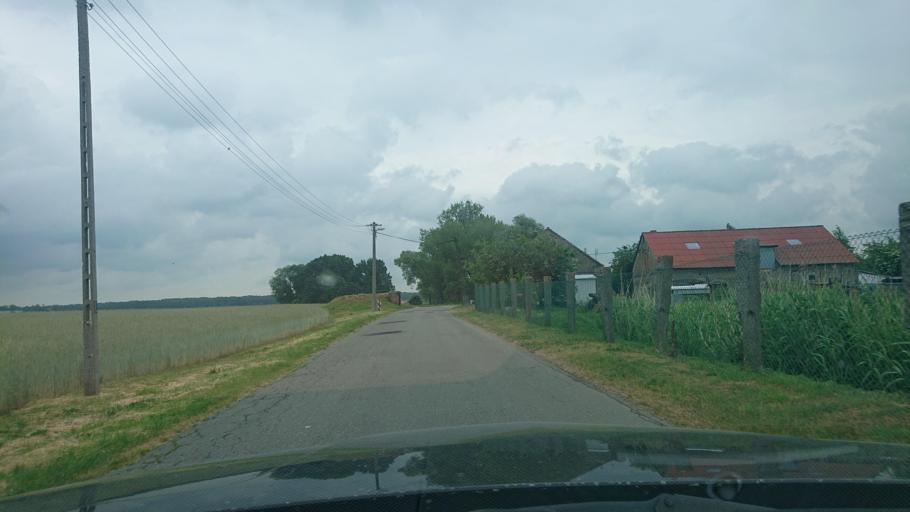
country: PL
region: Greater Poland Voivodeship
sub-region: Powiat gnieznienski
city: Gniezno
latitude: 52.4796
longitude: 17.5498
